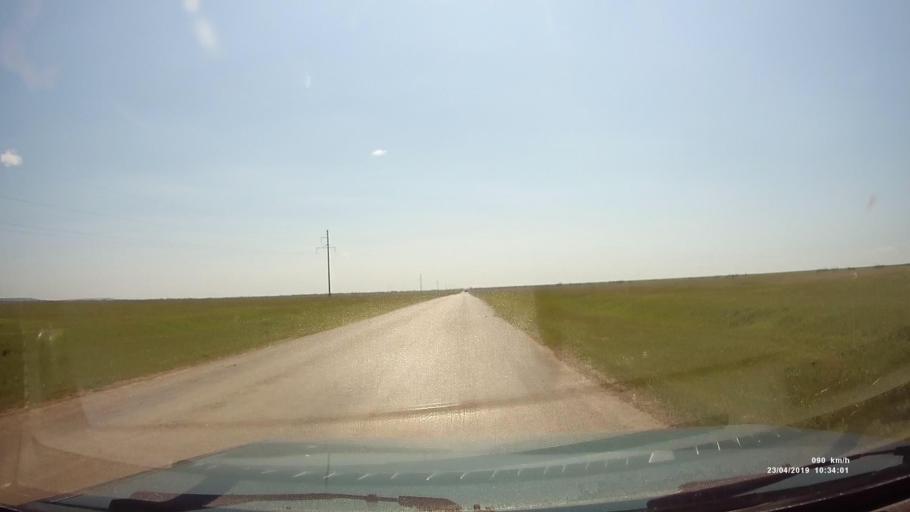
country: RU
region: Kalmykiya
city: Yashalta
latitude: 46.5680
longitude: 42.6049
